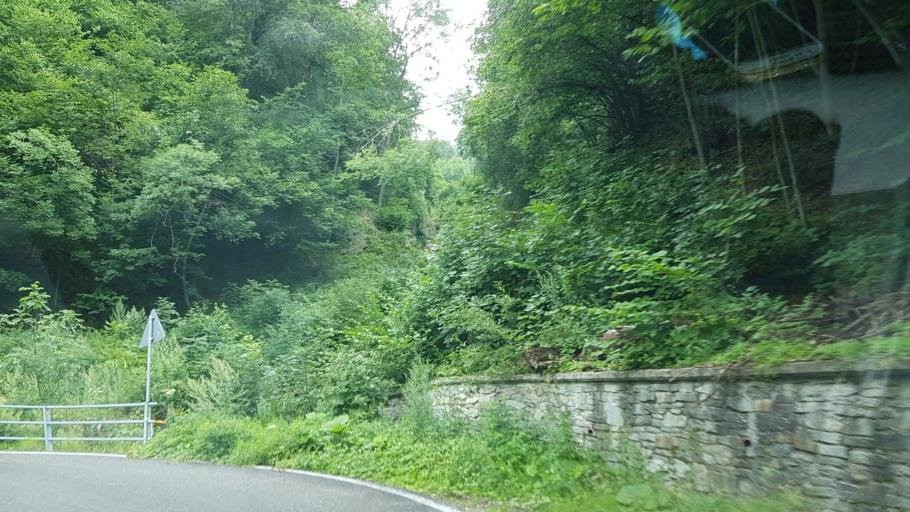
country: IT
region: Piedmont
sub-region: Provincia di Cuneo
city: Stroppo
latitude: 44.5220
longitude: 7.1242
